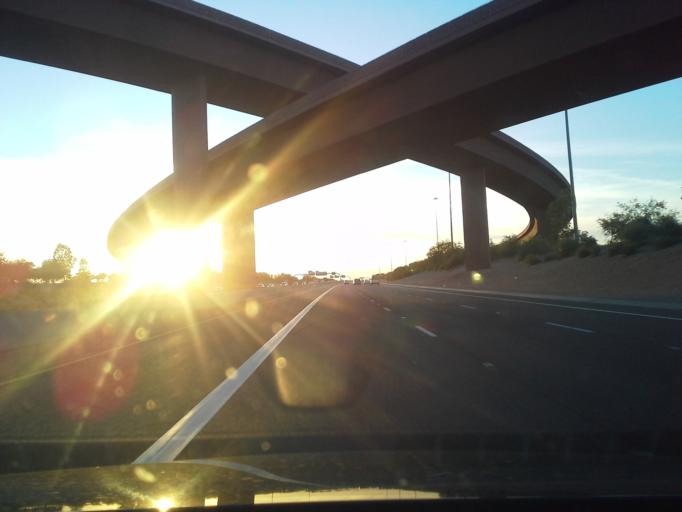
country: US
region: Arizona
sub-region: Pinal County
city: Apache Junction
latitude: 33.3868
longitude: -111.6483
